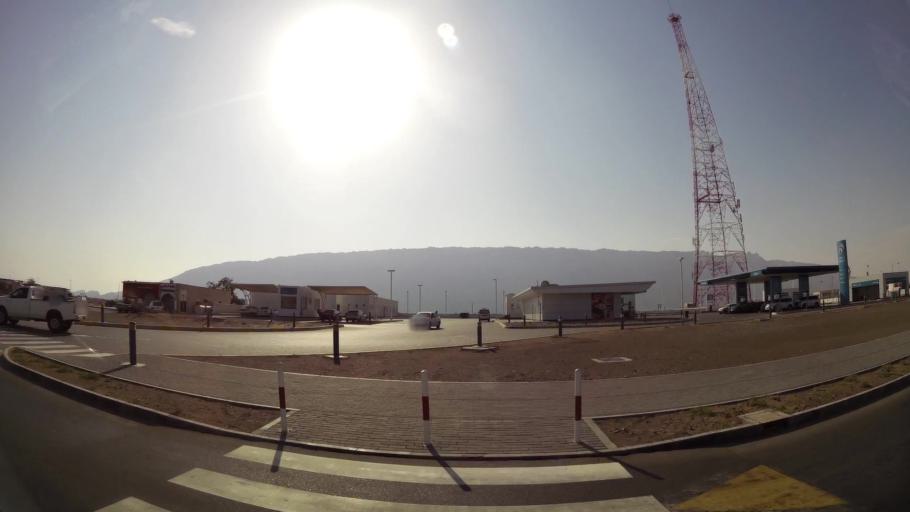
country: AE
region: Abu Dhabi
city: Al Ain
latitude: 24.0298
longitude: 55.8456
